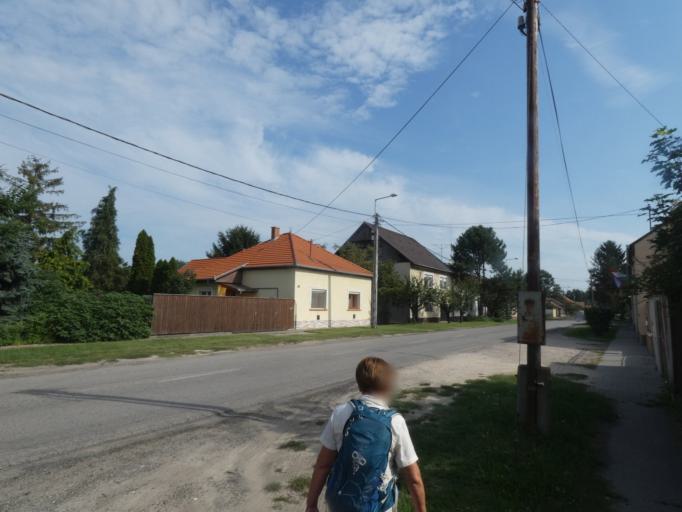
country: HU
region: Bacs-Kiskun
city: Lajosmizse
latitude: 47.0288
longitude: 19.5442
